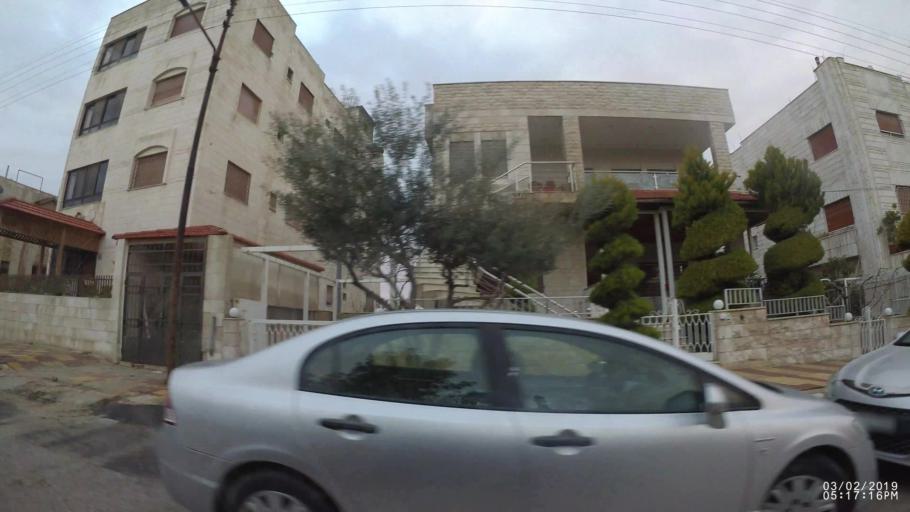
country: JO
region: Amman
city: Amman
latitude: 31.9844
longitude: 35.9128
